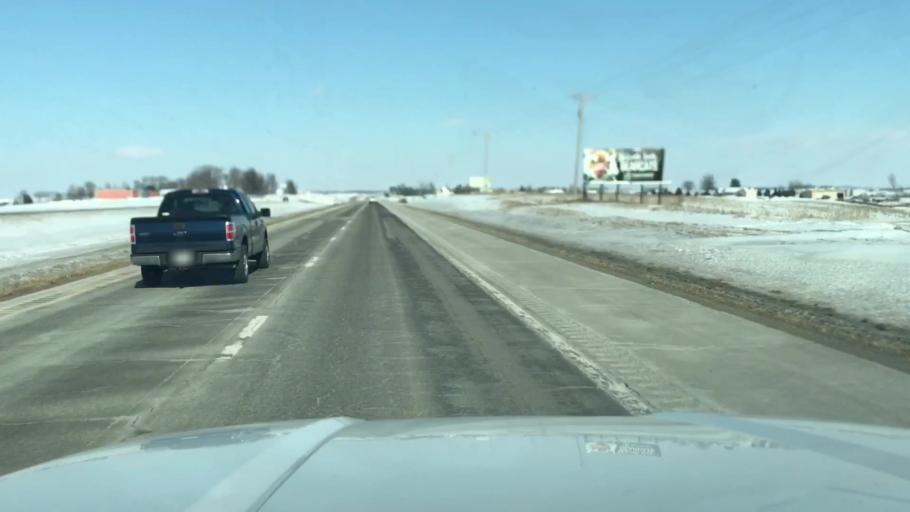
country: US
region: Missouri
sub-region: Nodaway County
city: Maryville
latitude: 40.2843
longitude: -94.8754
